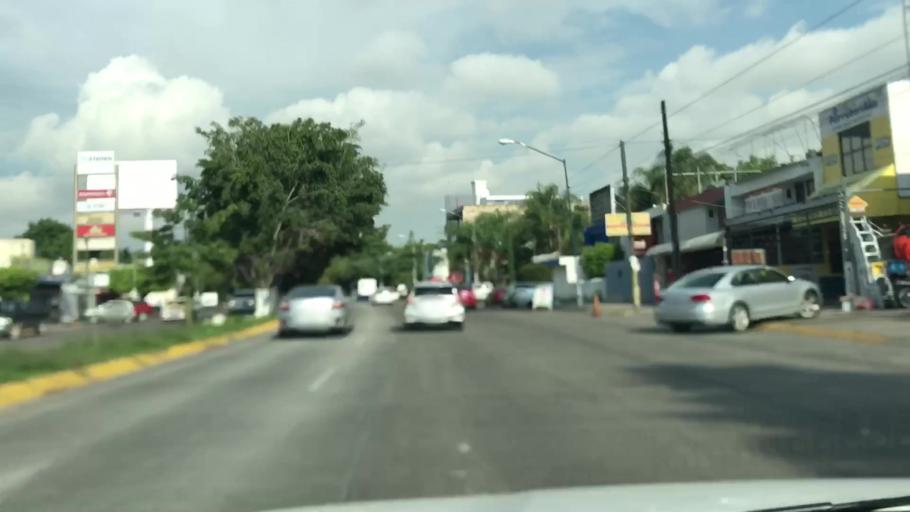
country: MX
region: Jalisco
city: Guadalajara
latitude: 20.6385
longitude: -103.4293
